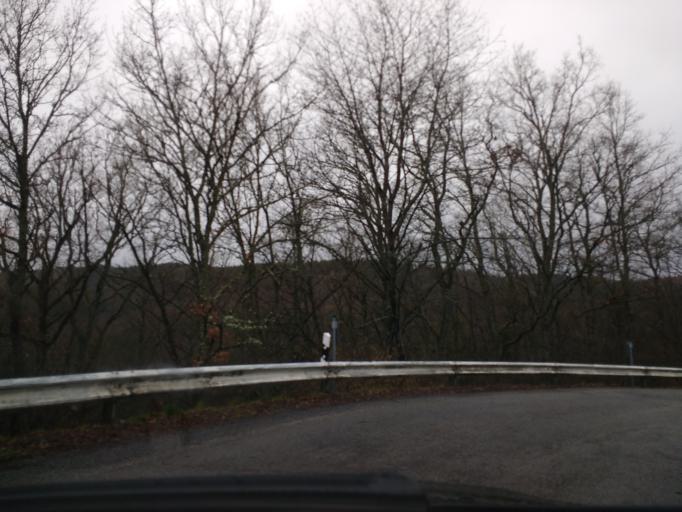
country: DE
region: Rheinland-Pfalz
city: Rascheid
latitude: 49.7193
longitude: 6.9321
